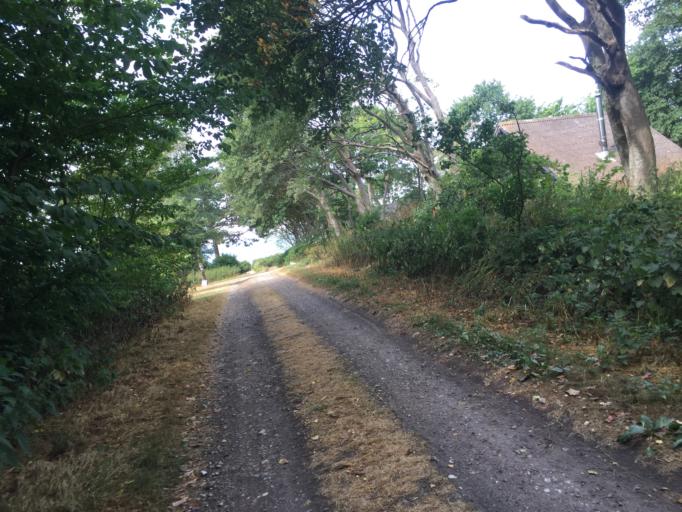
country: DK
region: Central Jutland
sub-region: Arhus Kommune
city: Beder
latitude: 55.9584
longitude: 10.4073
